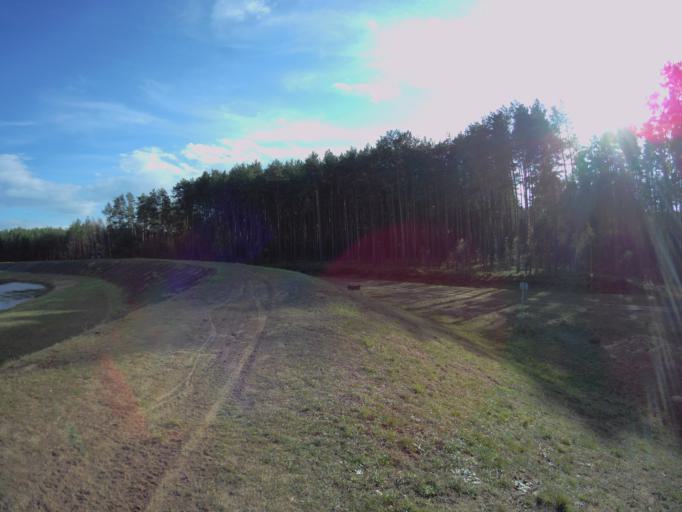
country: PL
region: Subcarpathian Voivodeship
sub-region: Powiat kolbuszowski
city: Lipnica
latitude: 50.3370
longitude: 21.9314
